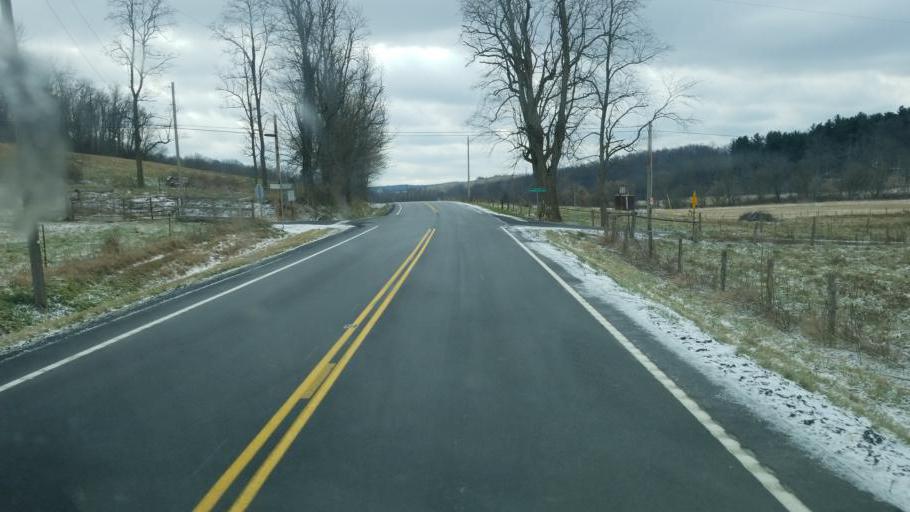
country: US
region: Ohio
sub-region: Muskingum County
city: Frazeysburg
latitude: 40.1533
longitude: -82.2182
